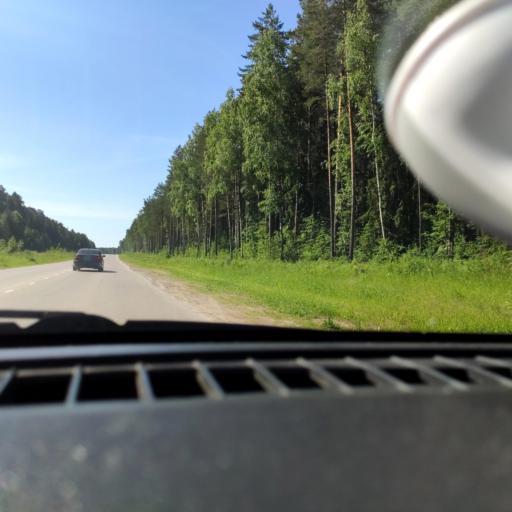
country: RU
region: Perm
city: Overyata
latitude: 58.0061
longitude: 55.8766
